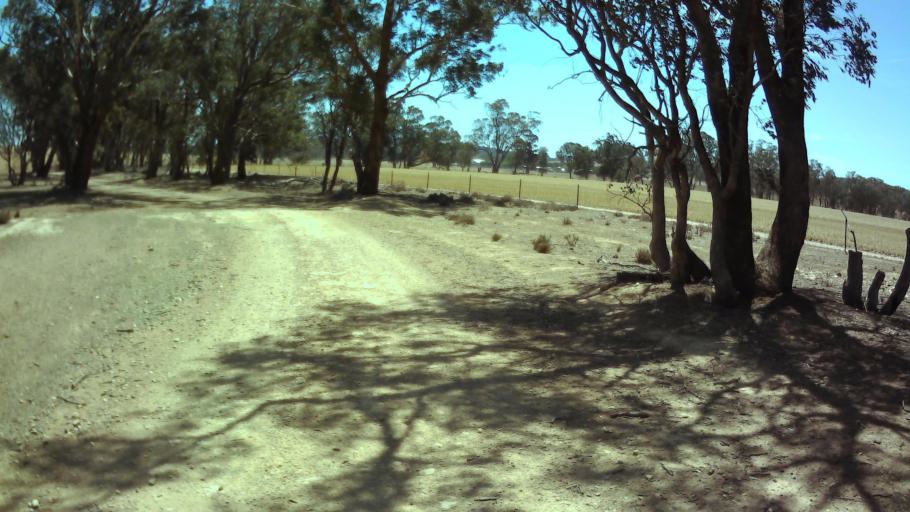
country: AU
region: New South Wales
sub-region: Weddin
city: Grenfell
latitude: -33.9806
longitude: 148.1690
